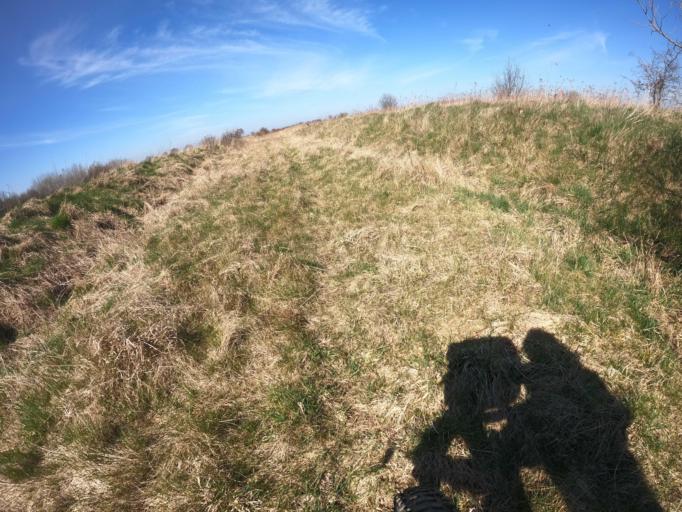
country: PL
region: West Pomeranian Voivodeship
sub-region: Powiat gryficki
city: Brojce
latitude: 53.9855
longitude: 15.3878
